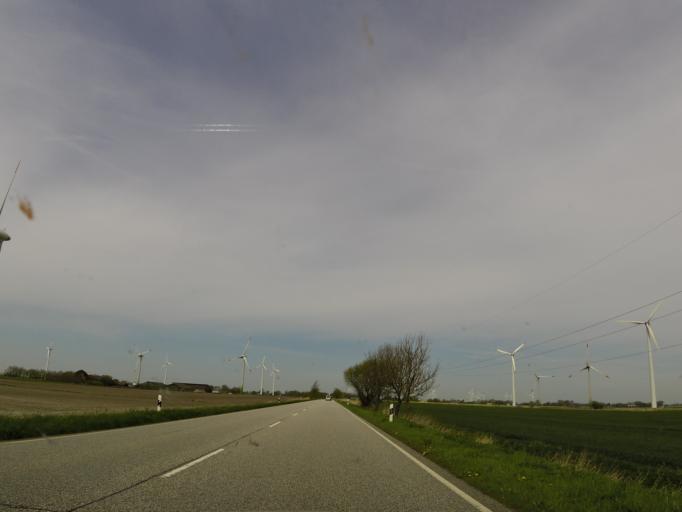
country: DE
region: Schleswig-Holstein
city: Stelle-Wittenwurth
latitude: 54.2649
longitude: 9.0287
